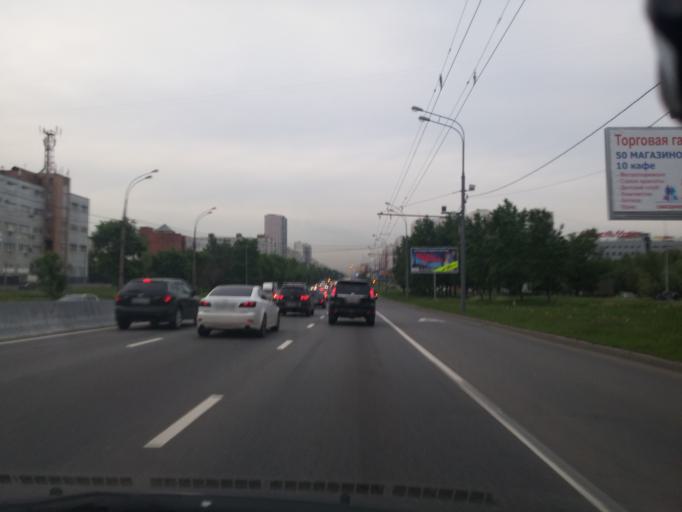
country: RU
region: Moscow
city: Altuf'yevskiy
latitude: 55.8852
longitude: 37.5868
